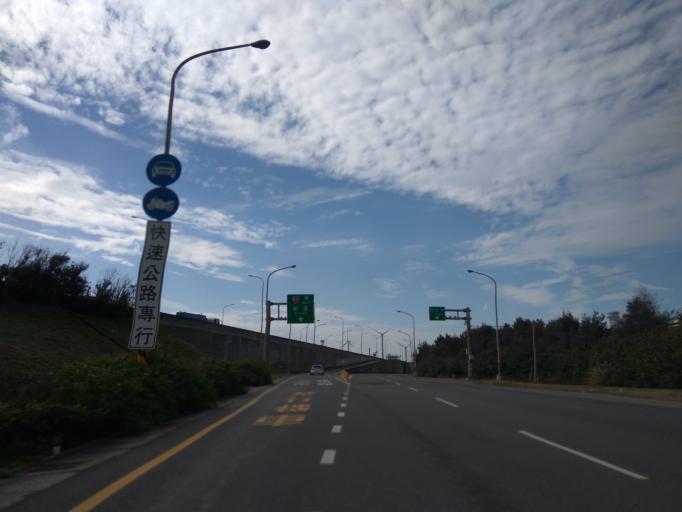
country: TW
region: Taiwan
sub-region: Hsinchu
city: Zhubei
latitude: 25.0289
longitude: 121.0523
